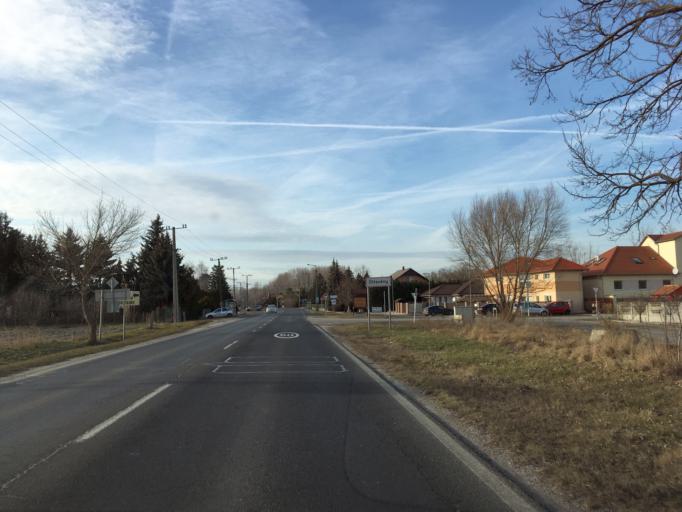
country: HU
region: Gyor-Moson-Sopron
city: Otteveny
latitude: 47.7198
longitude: 17.5050
